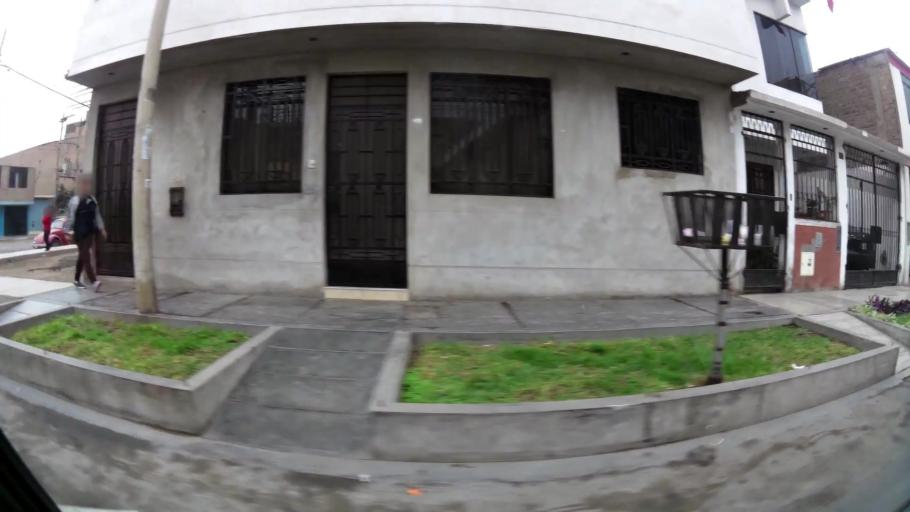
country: PE
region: Lima
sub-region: Lima
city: Independencia
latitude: -11.9680
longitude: -77.0801
